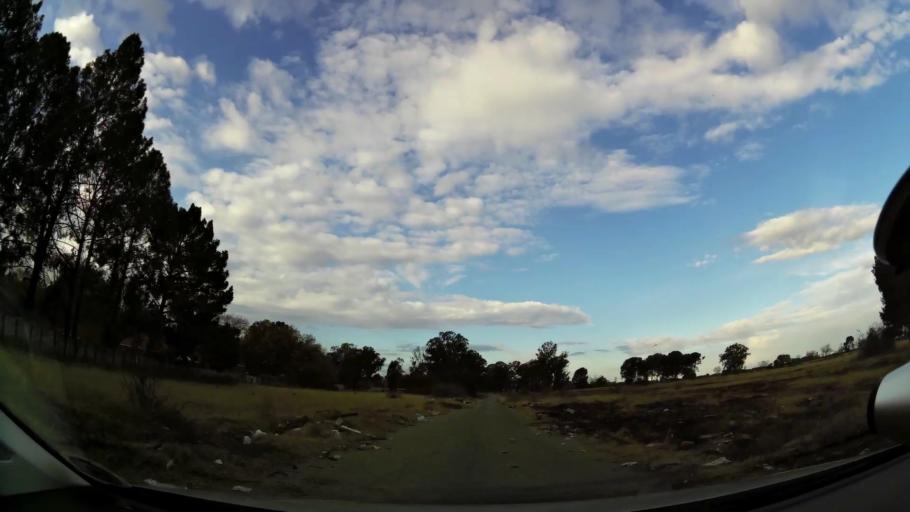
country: ZA
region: Orange Free State
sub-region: Lejweleputswa District Municipality
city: Welkom
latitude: -28.0011
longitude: 26.7122
